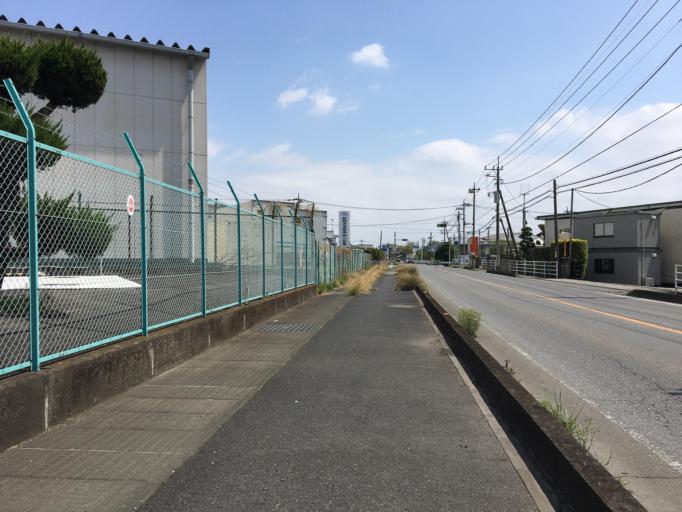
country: JP
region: Gunma
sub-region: Sawa-gun
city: Tamamura
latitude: 36.2913
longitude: 139.1459
